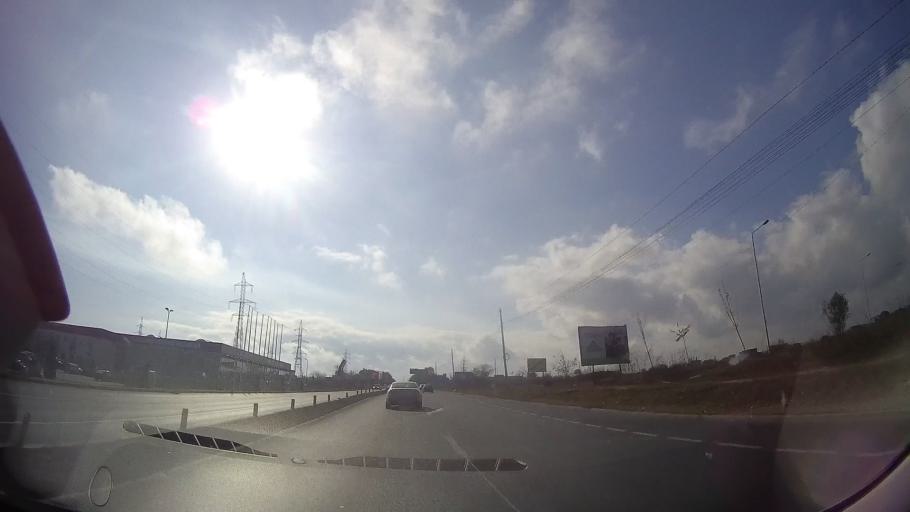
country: RO
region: Constanta
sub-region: Municipiul Constanta
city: Constanta
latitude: 44.1350
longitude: 28.6193
